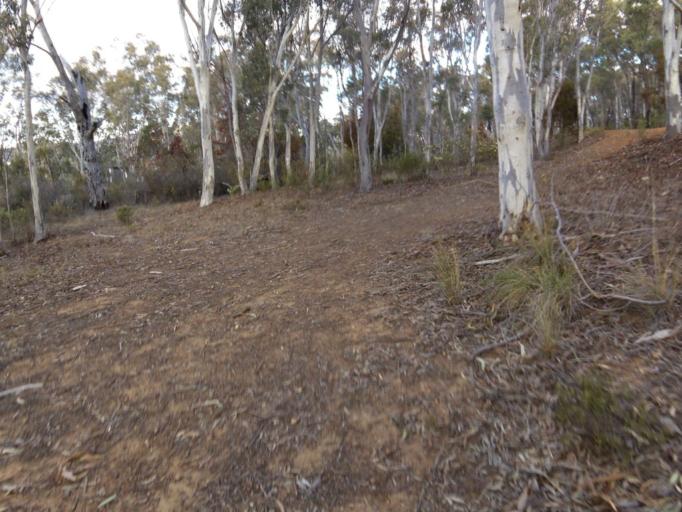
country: AU
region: Australian Capital Territory
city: Acton
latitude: -35.2609
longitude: 149.1101
